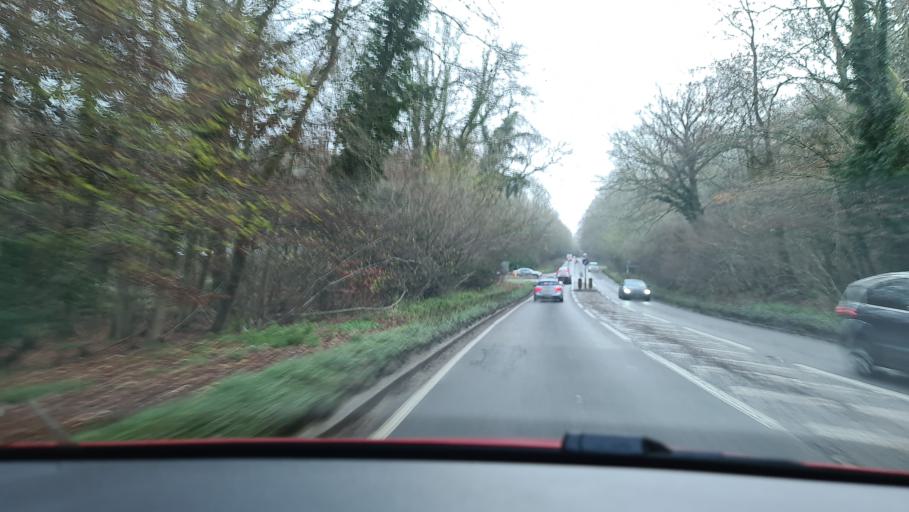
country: GB
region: England
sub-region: Buckinghamshire
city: Seer Green
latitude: 51.5984
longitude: -0.6108
